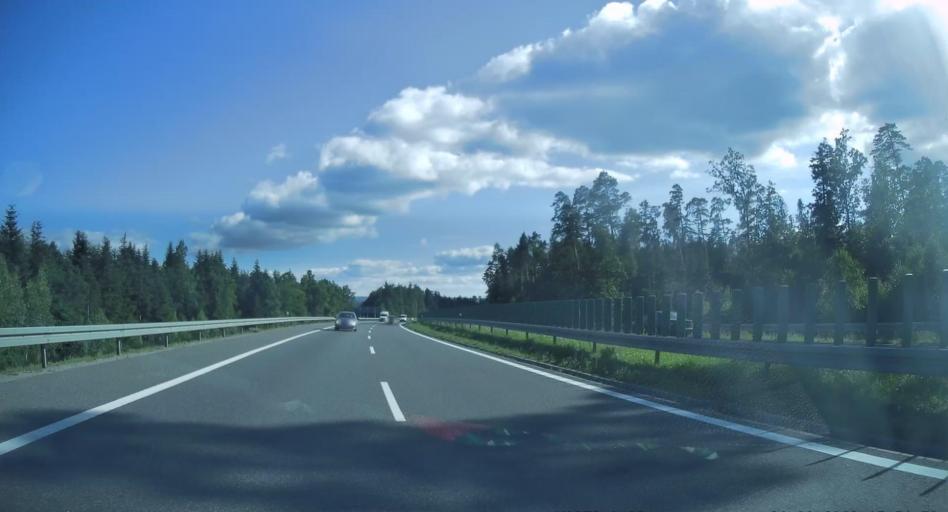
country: PL
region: Swietokrzyskie
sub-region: Powiat skarzyski
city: Suchedniow
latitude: 51.0733
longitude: 20.8368
